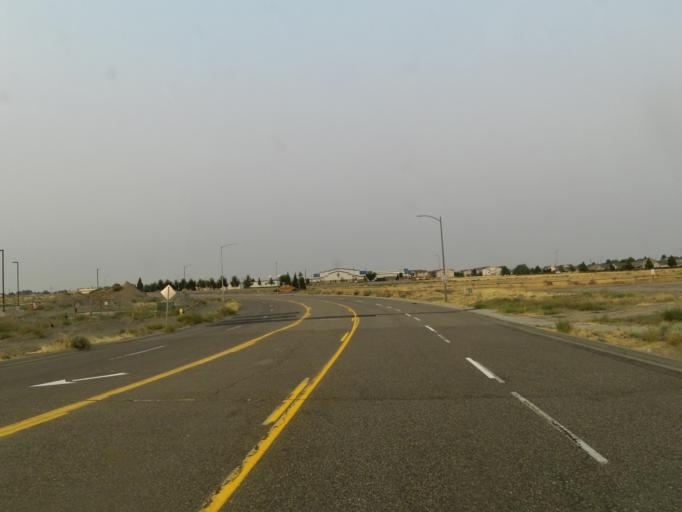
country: US
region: Washington
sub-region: Franklin County
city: West Pasco
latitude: 46.2721
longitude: -119.2210
